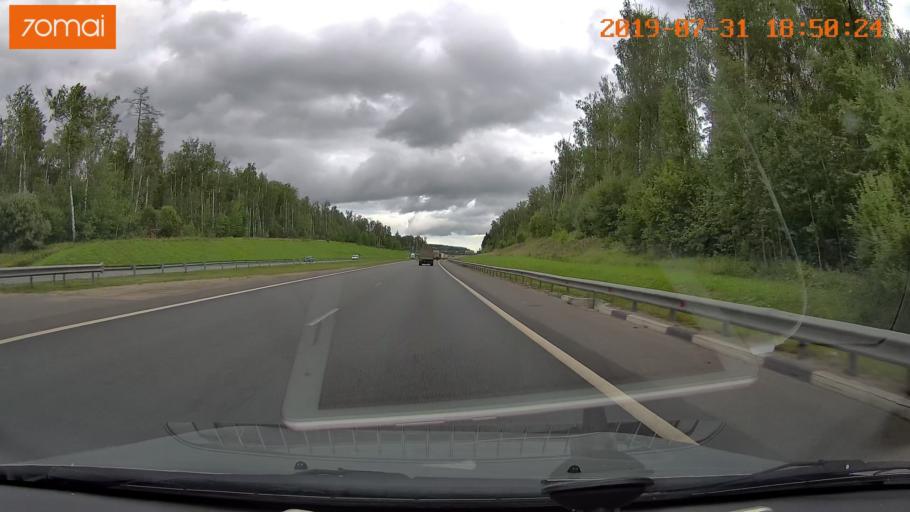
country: RU
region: Moskovskaya
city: Troitskoye
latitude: 55.2289
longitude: 38.5812
